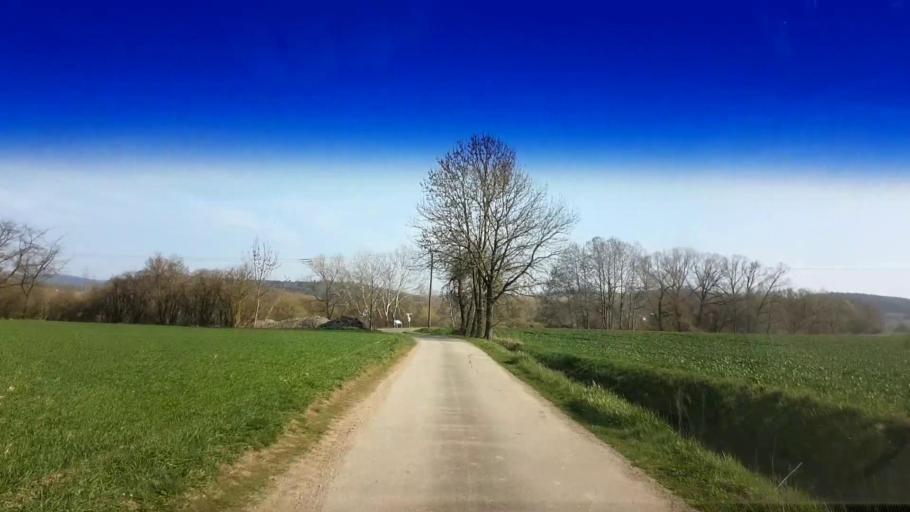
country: DE
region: Bavaria
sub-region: Upper Franconia
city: Ebensfeld
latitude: 50.0499
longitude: 10.9329
